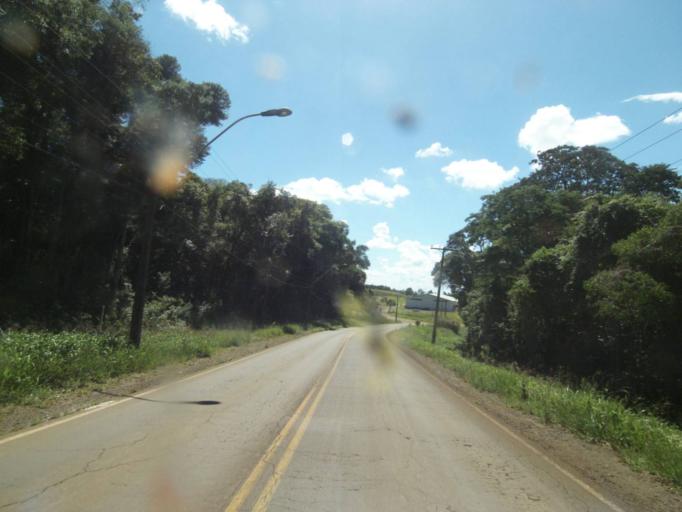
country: BR
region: Parana
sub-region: Chopinzinho
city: Chopinzinho
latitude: -25.7910
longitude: -52.0923
